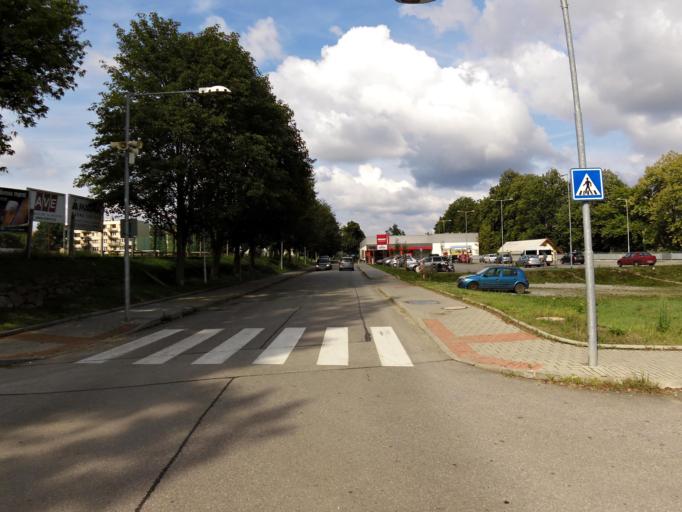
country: CZ
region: Jihocesky
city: Suchdol nad Luznici
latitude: 48.8917
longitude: 14.8790
